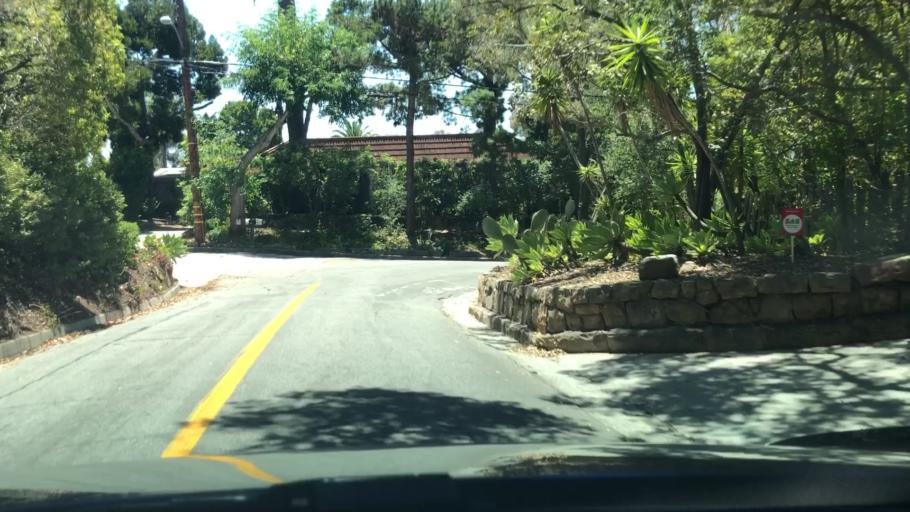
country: US
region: California
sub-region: Santa Barbara County
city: Mission Canyon
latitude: 34.4401
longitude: -119.7103
